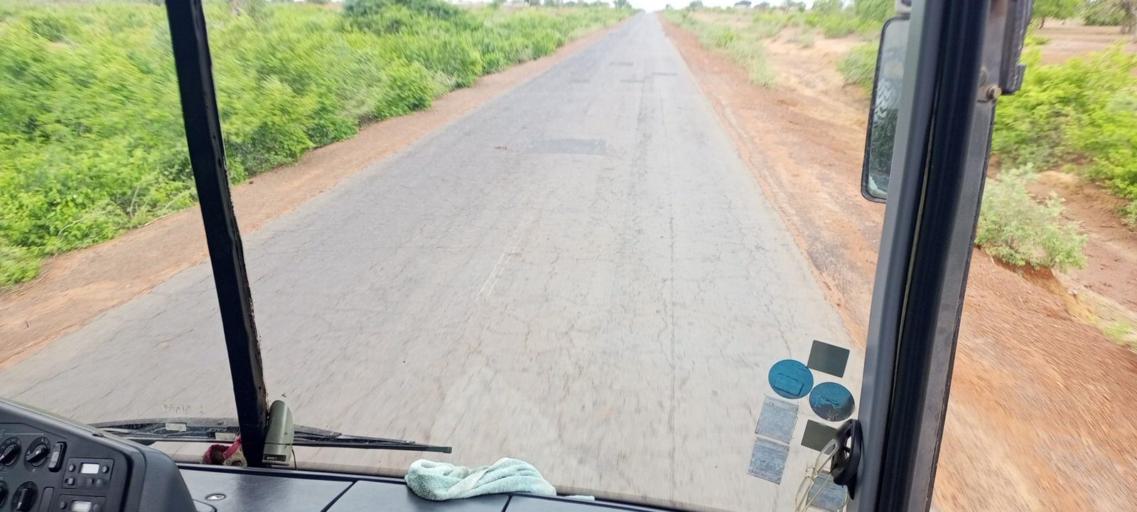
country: ML
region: Segou
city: Bla
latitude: 12.7228
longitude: -5.7251
